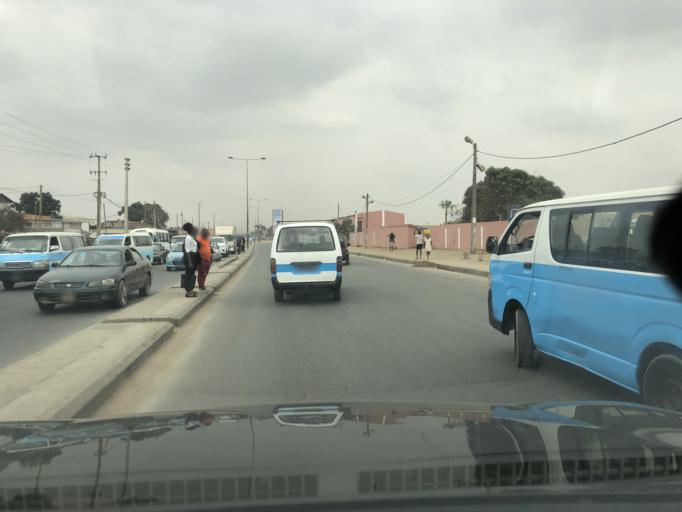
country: AO
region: Luanda
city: Luanda
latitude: -8.8225
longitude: 13.2822
